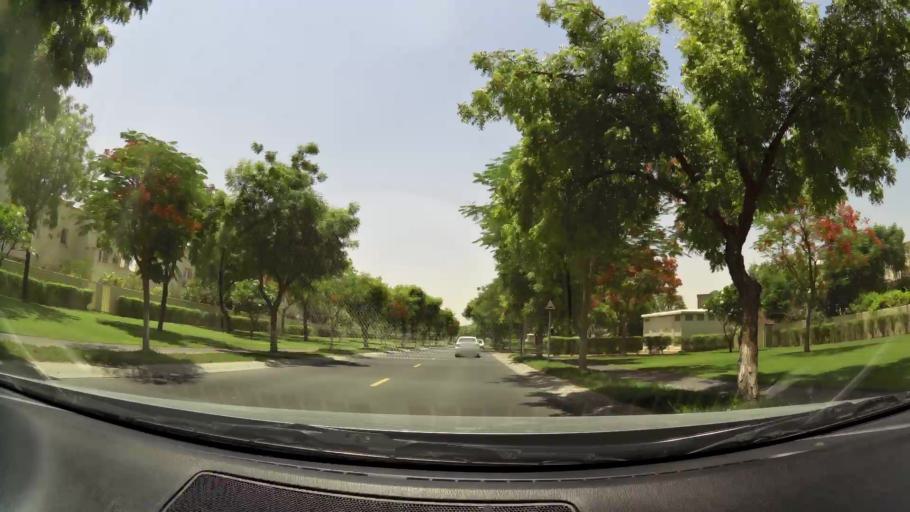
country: AE
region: Dubai
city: Dubai
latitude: 25.0549
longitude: 55.1806
